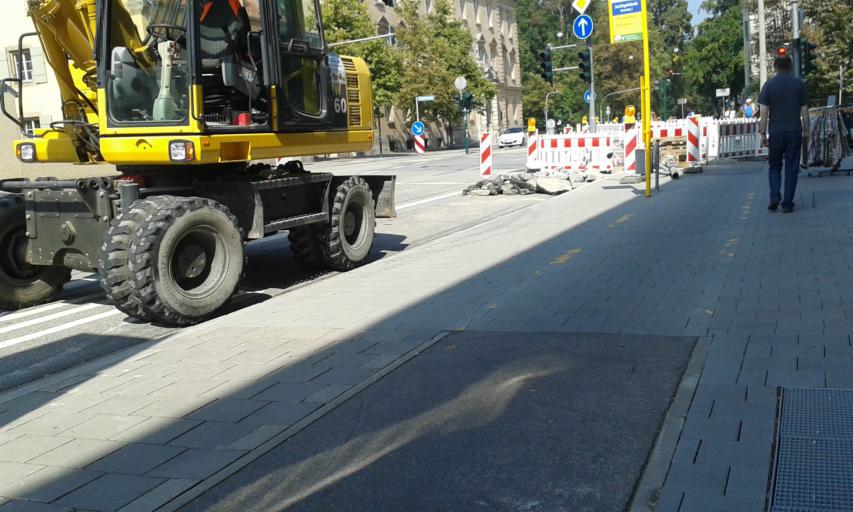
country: DE
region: Bavaria
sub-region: Upper Palatinate
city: Lappersdorf
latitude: 49.0135
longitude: 12.0885
